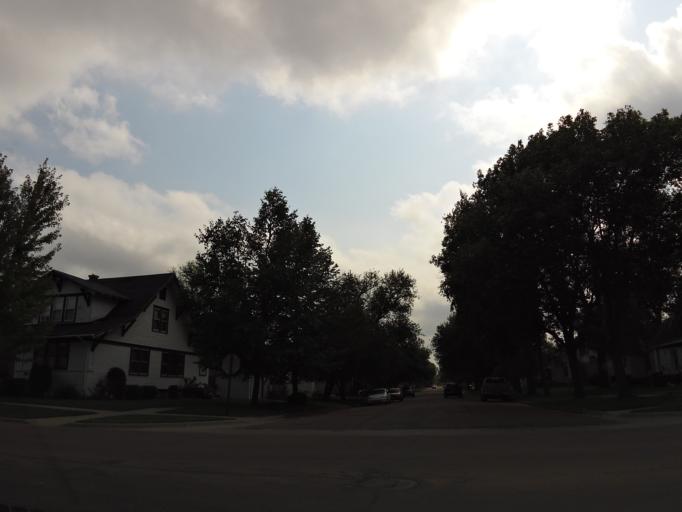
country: US
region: South Dakota
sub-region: Codington County
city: Watertown
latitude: 44.8963
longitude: -97.1180
